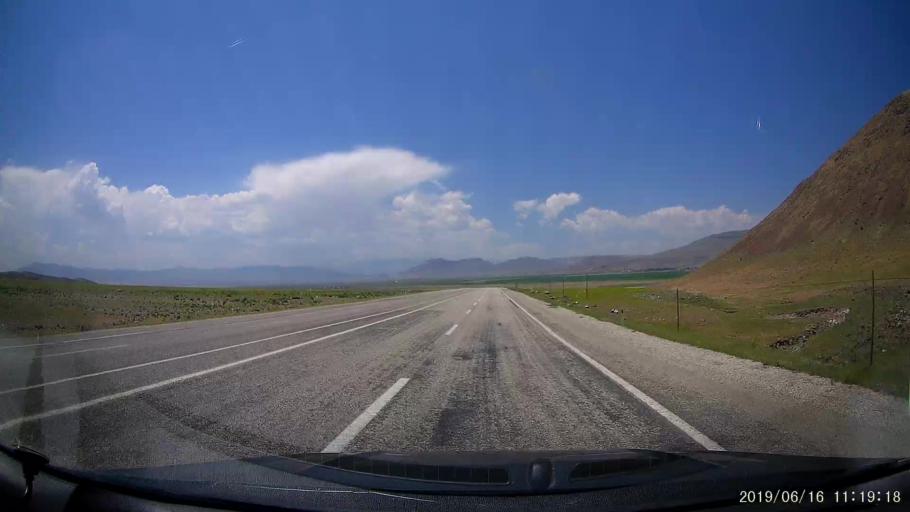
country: TR
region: Agri
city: Dogubayazit
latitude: 39.7002
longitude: 44.1157
